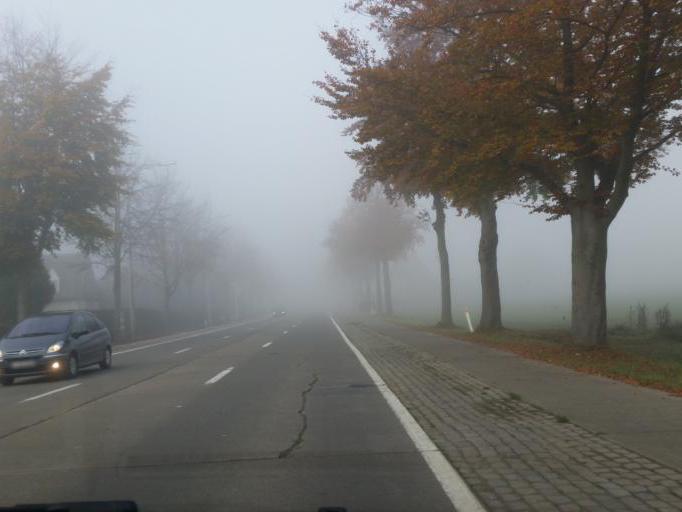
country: BE
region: Flanders
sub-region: Provincie Oost-Vlaanderen
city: Lede
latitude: 50.9502
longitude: 3.9362
